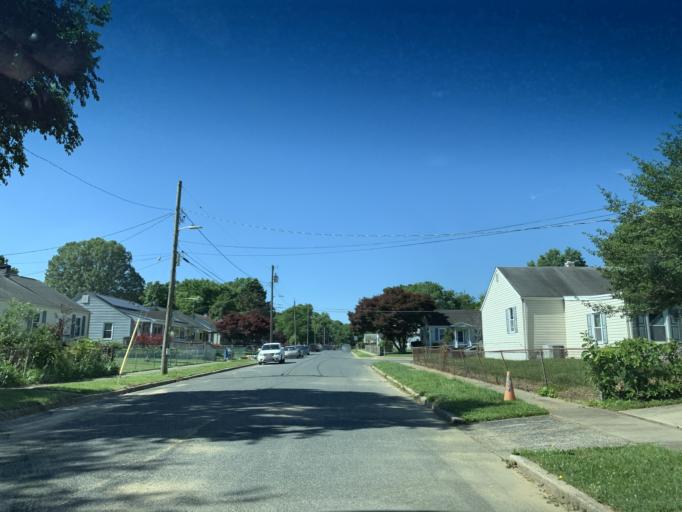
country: US
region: Maryland
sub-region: Harford County
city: Aberdeen
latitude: 39.5051
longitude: -76.1614
